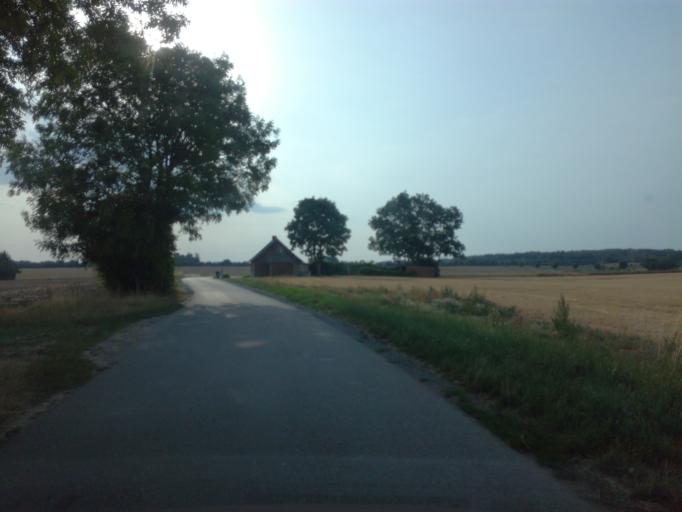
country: DK
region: South Denmark
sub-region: Vejle Kommune
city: Borkop
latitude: 55.6400
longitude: 9.6130
